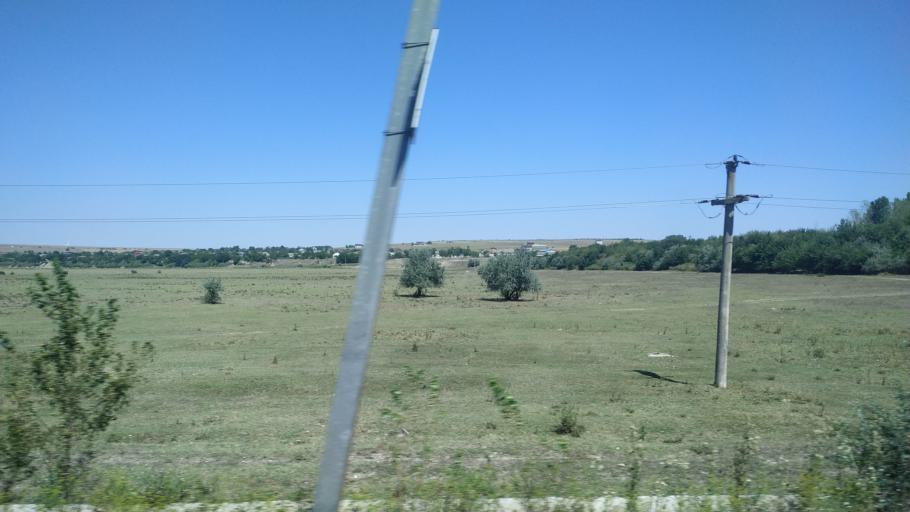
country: RO
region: Constanta
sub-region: Comuna Mircea Voda
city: Satu Nou
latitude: 44.2571
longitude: 28.2316
